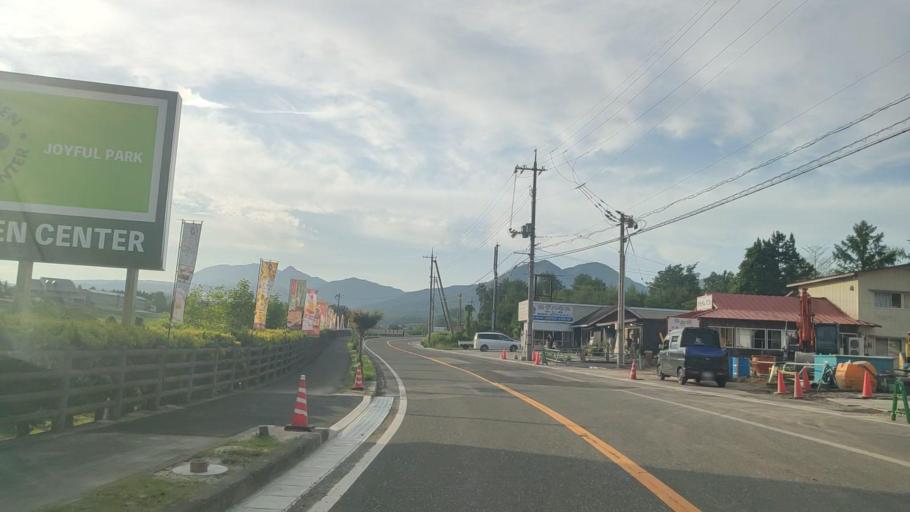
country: JP
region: Tottori
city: Kurayoshi
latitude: 35.2913
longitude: 133.6364
